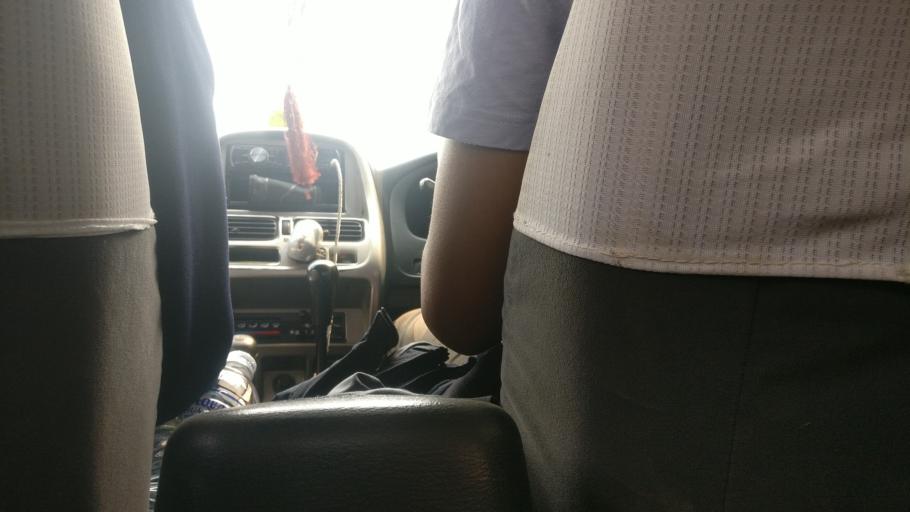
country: NP
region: Central Region
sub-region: Bagmati Zone
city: Kathmandu
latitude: 27.6942
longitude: 85.3216
